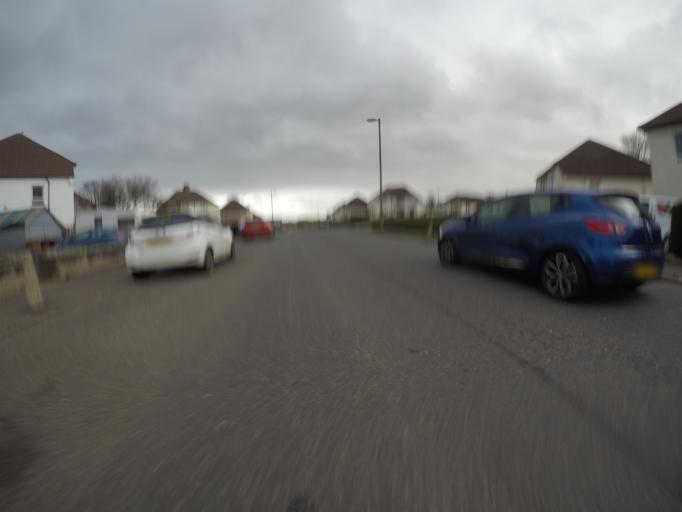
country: GB
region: Scotland
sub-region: East Ayrshire
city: Kilmarnock
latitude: 55.6122
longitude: -4.5156
